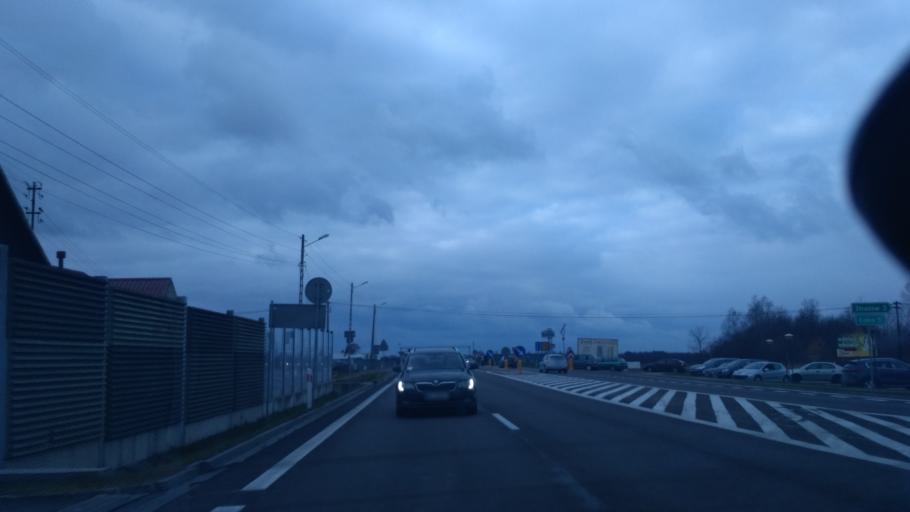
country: PL
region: Subcarpathian Voivodeship
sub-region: Powiat rzeszowski
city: Krasne
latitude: 50.0436
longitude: 22.1229
